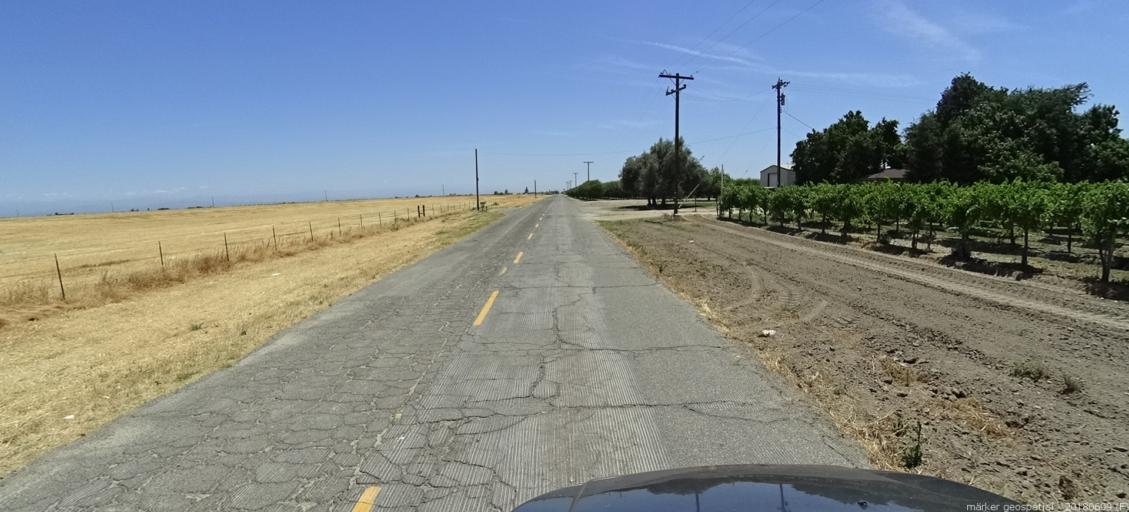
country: US
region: California
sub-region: Madera County
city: Madera
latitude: 36.9382
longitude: -120.1797
